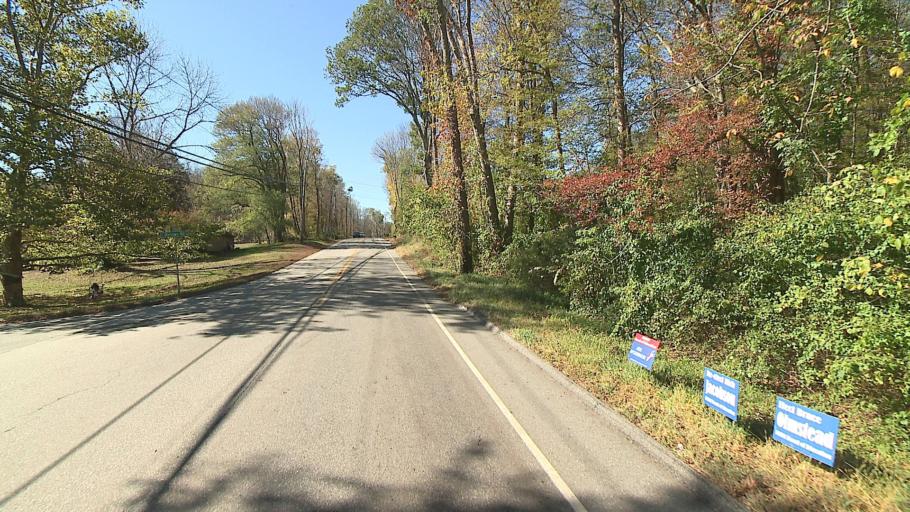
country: US
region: Connecticut
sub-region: Tolland County
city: Hebron
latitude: 41.6528
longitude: -72.3873
